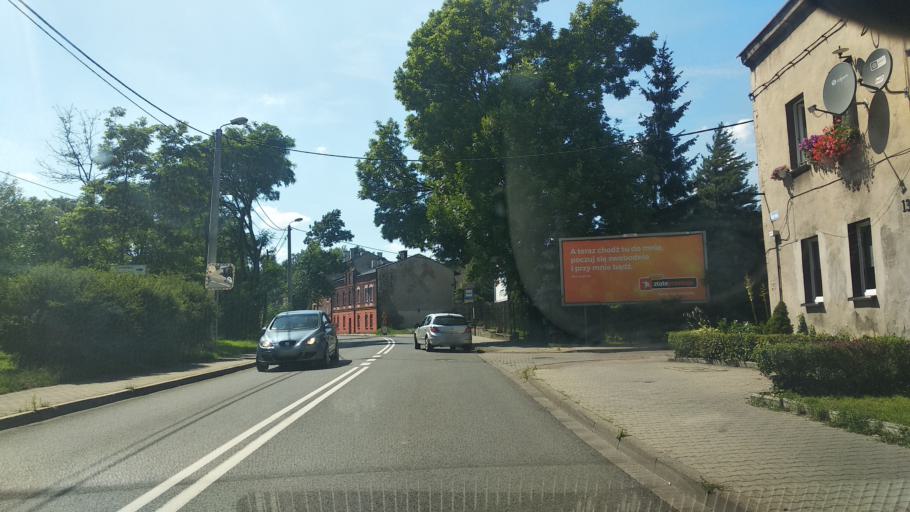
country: PL
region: Silesian Voivodeship
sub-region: Sosnowiec
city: Sosnowiec
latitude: 50.2661
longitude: 19.0894
